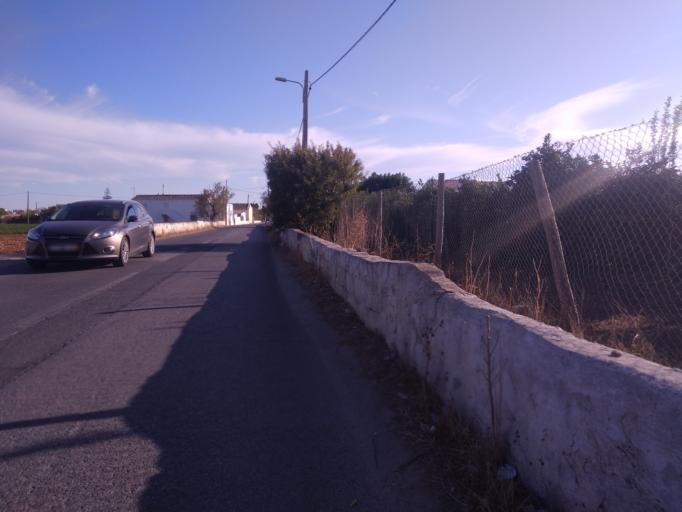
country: PT
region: Faro
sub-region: Faro
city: Faro
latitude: 37.0495
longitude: -7.9375
